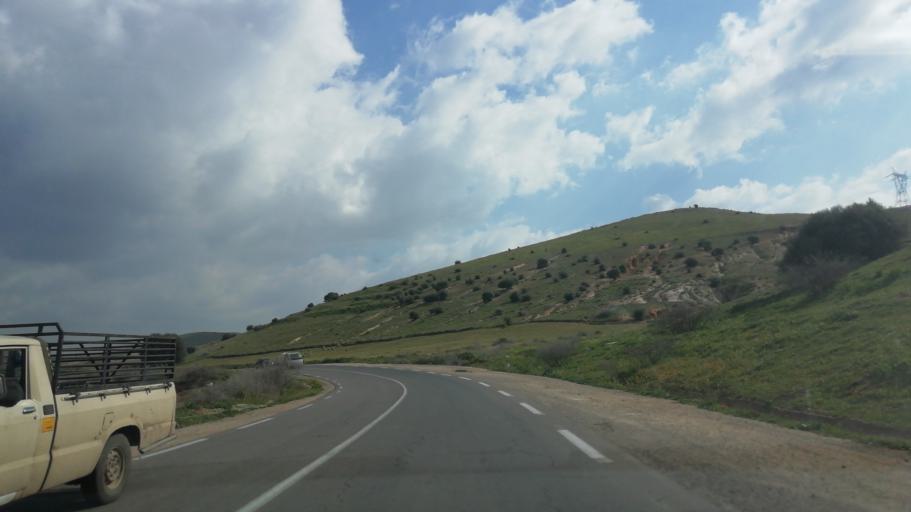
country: DZ
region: Mostaganem
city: Mostaganem
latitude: 35.7027
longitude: 0.2302
